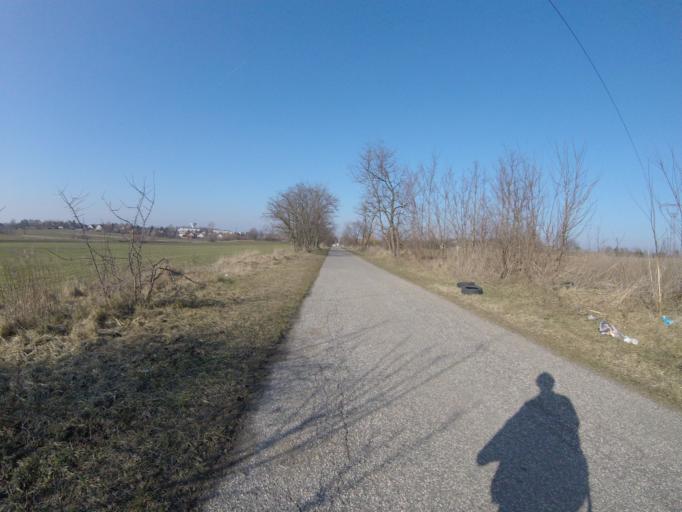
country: HU
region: Komarom-Esztergom
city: Oroszlany
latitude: 47.4769
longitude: 18.3310
